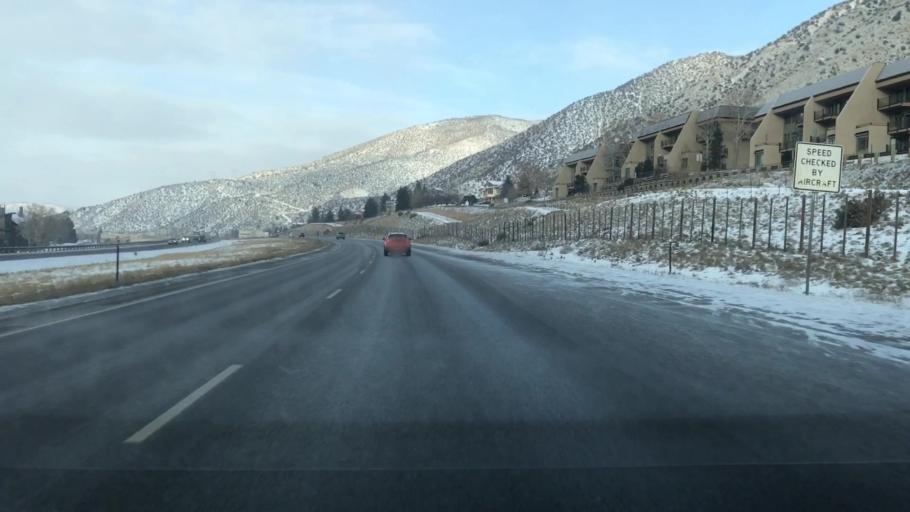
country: US
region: Colorado
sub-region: Eagle County
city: Avon
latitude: 39.6399
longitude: -106.5265
